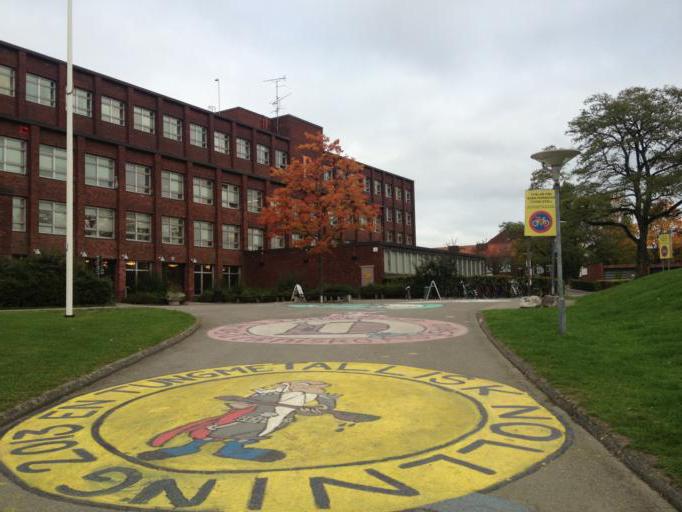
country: SE
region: Skane
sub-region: Lunds Kommun
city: Lund
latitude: 55.7104
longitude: 13.2074
